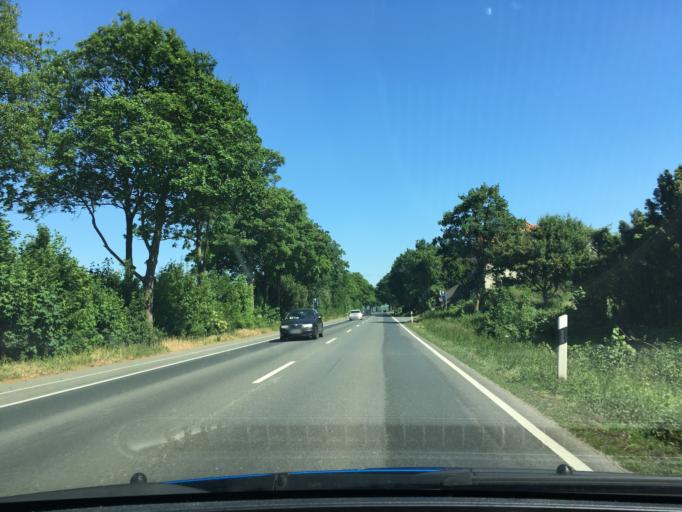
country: DE
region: Lower Saxony
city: Beckedorf
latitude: 52.3376
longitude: 9.3231
